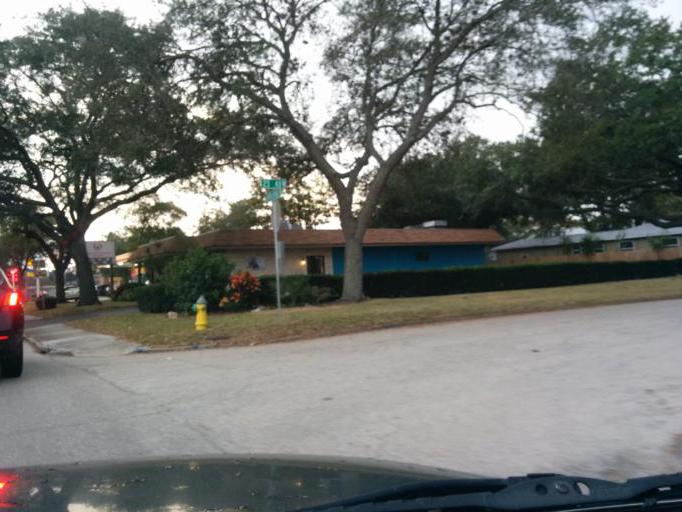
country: US
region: Florida
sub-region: Pinellas County
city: Saint Petersburg
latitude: 27.7931
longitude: -82.6468
